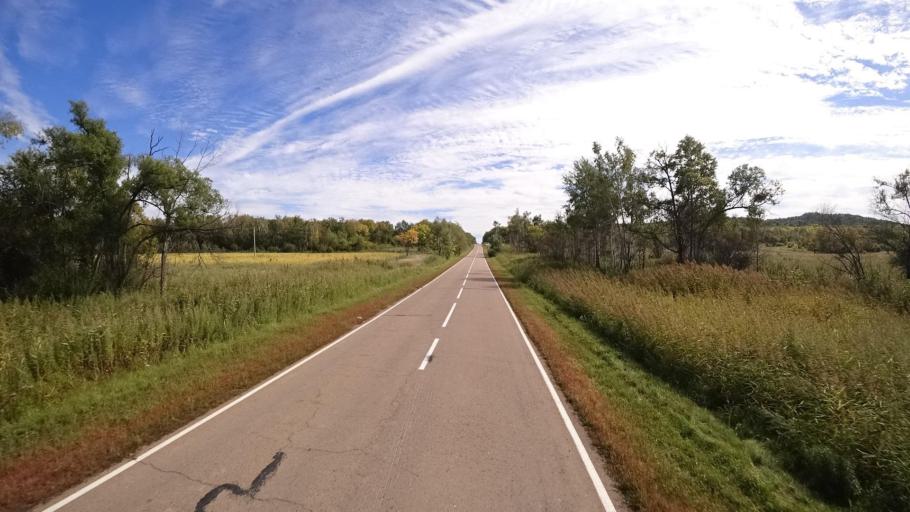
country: RU
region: Primorskiy
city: Yakovlevka
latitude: 44.4094
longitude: 133.5898
